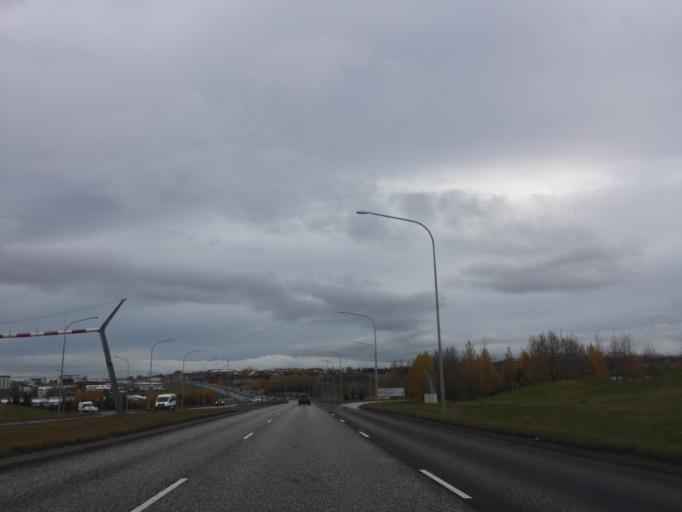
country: IS
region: Capital Region
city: Reykjavik
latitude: 64.1260
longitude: -21.8547
